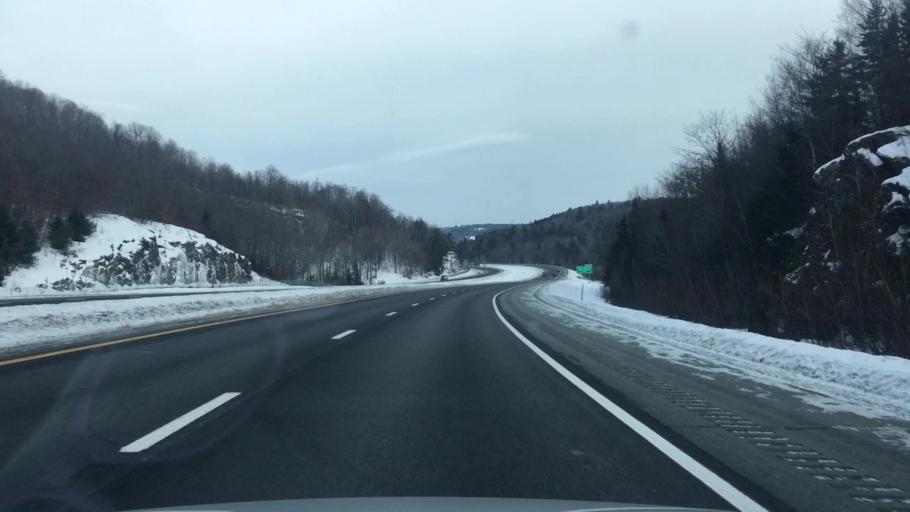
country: US
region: New Hampshire
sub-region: Grafton County
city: Enfield
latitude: 43.5761
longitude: -72.1604
